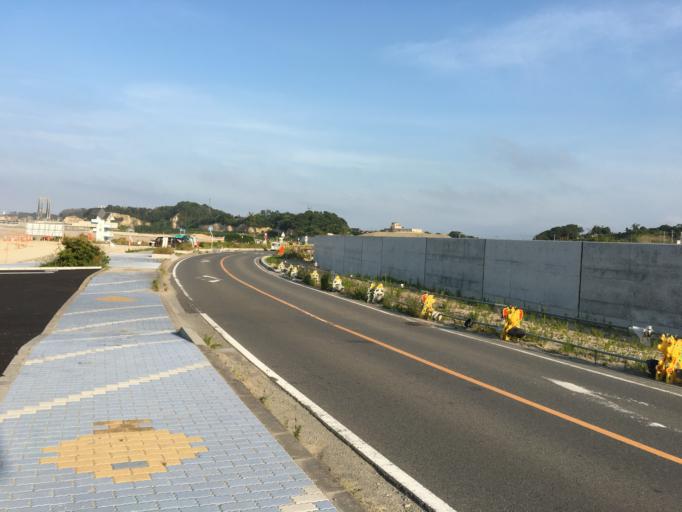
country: JP
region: Miyagi
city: Marumori
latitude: 37.8297
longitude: 140.9640
